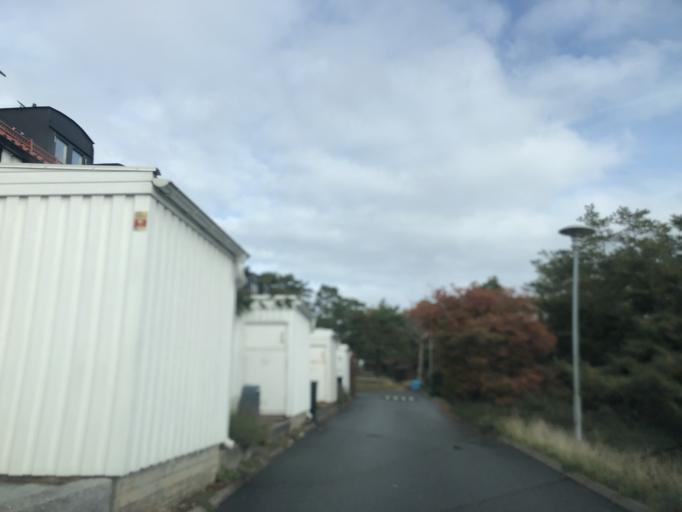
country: SE
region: Vaestra Goetaland
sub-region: Goteborg
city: Majorna
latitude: 57.6682
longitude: 11.8961
